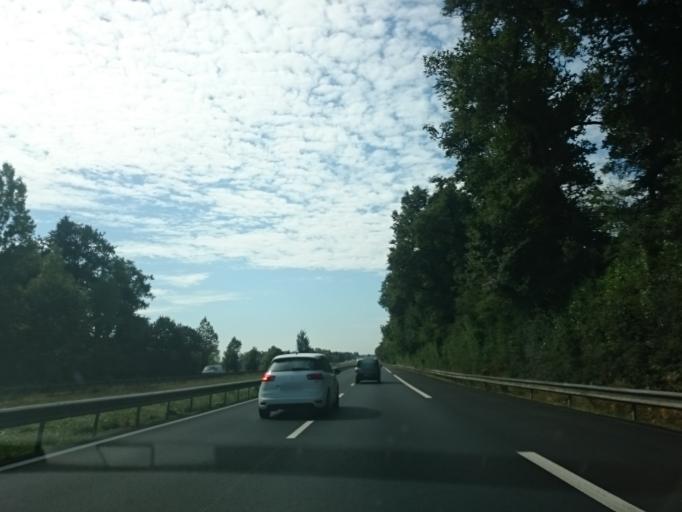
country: FR
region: Pays de la Loire
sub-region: Departement de la Loire-Atlantique
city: La Grigonnais
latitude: 47.5023
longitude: -1.6389
